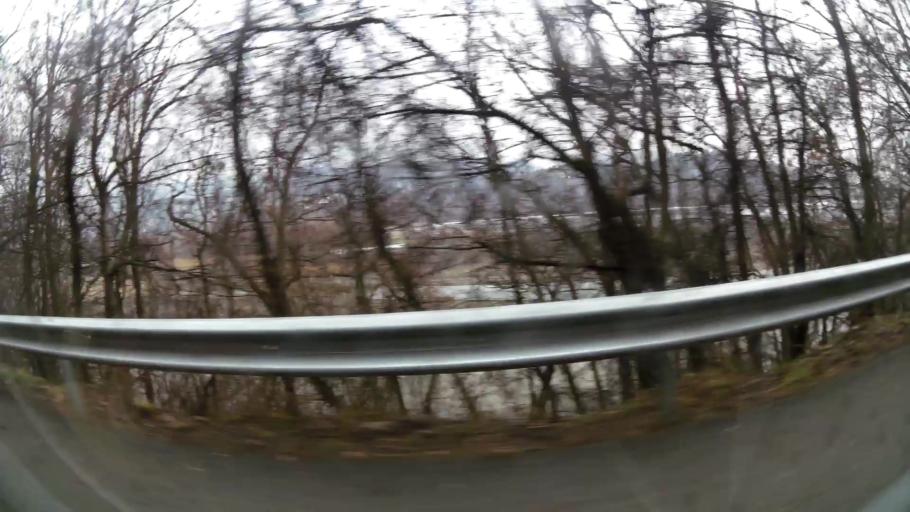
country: BG
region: Sofia-Capital
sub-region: Stolichna Obshtina
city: Sofia
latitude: 42.5906
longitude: 23.4244
